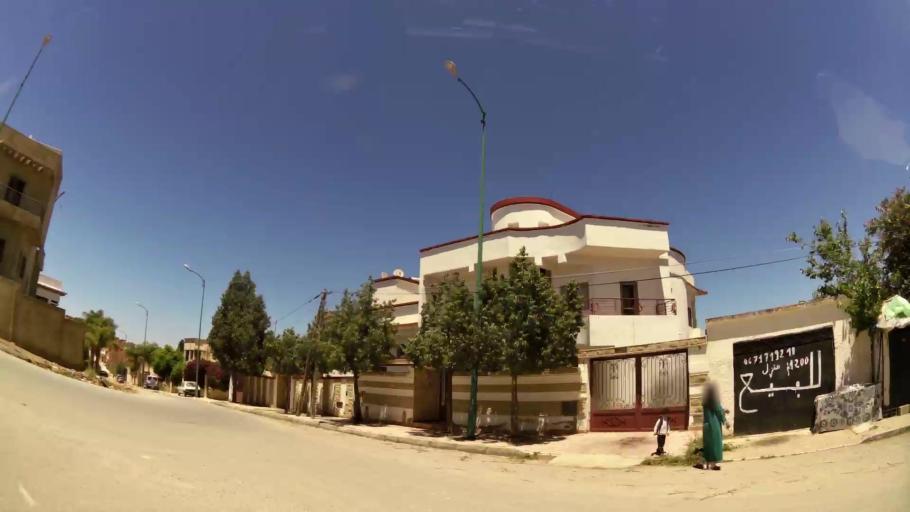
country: MA
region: Meknes-Tafilalet
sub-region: Meknes
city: Meknes
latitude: 33.9039
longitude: -5.5564
